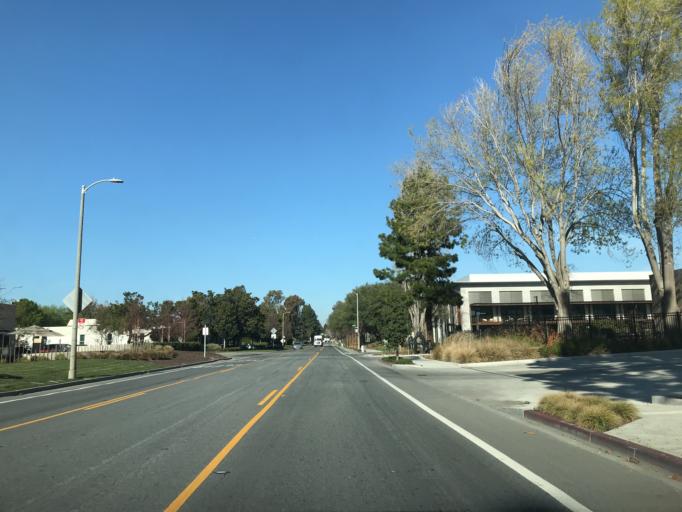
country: US
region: California
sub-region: Santa Clara County
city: Sunnyvale
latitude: 37.4090
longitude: -122.0234
